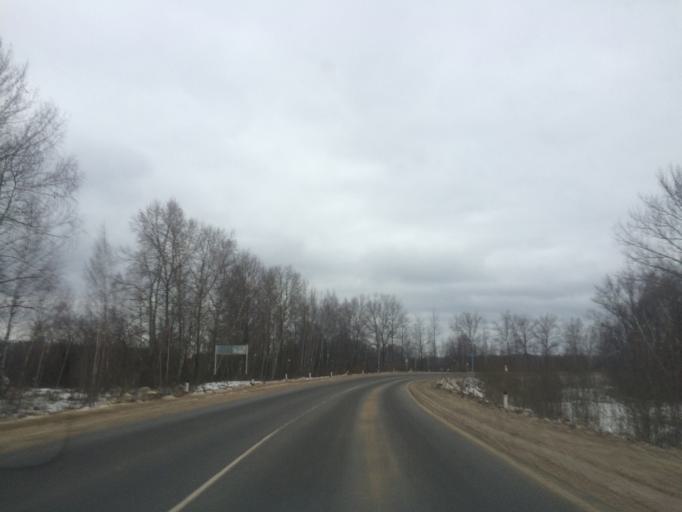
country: RU
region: Tula
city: Odoyev
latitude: 53.9961
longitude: 36.7567
